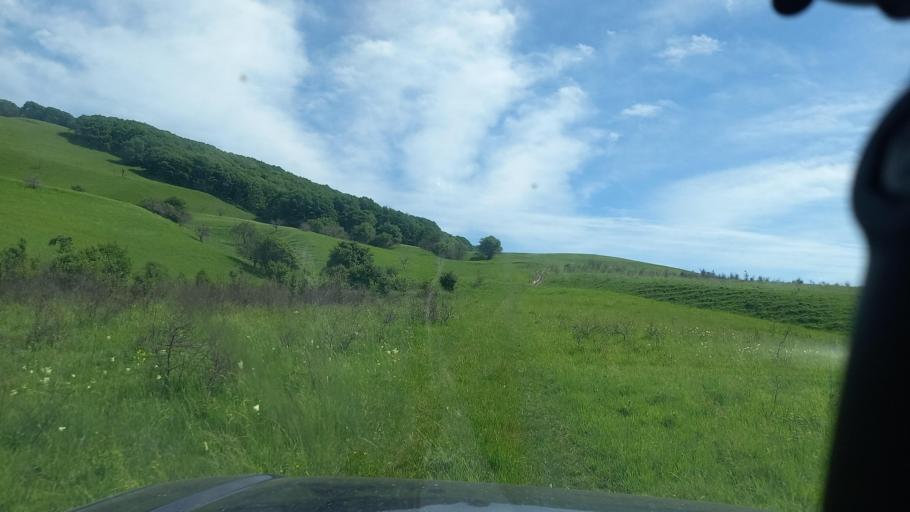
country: RU
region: Karachayevo-Cherkesiya
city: Kurdzhinovo
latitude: 44.1468
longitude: 41.0683
